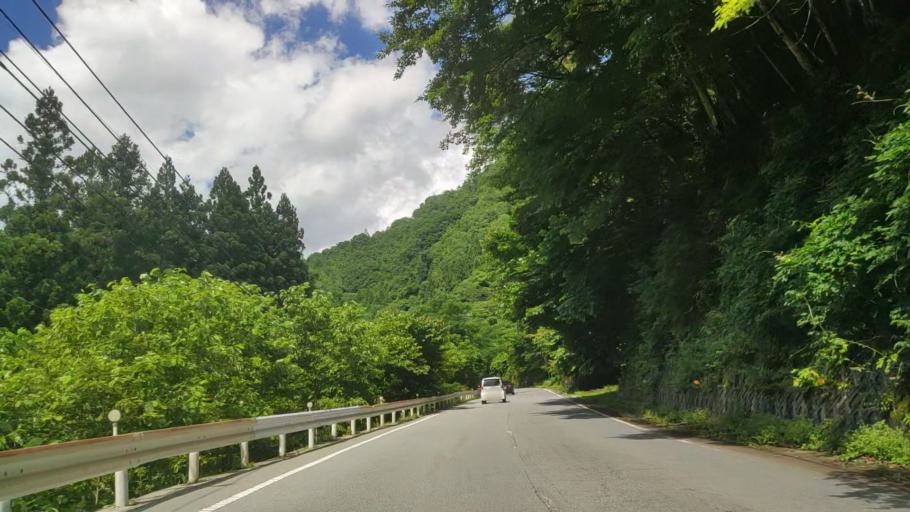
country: JP
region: Yamanashi
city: Enzan
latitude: 35.8273
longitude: 138.7640
